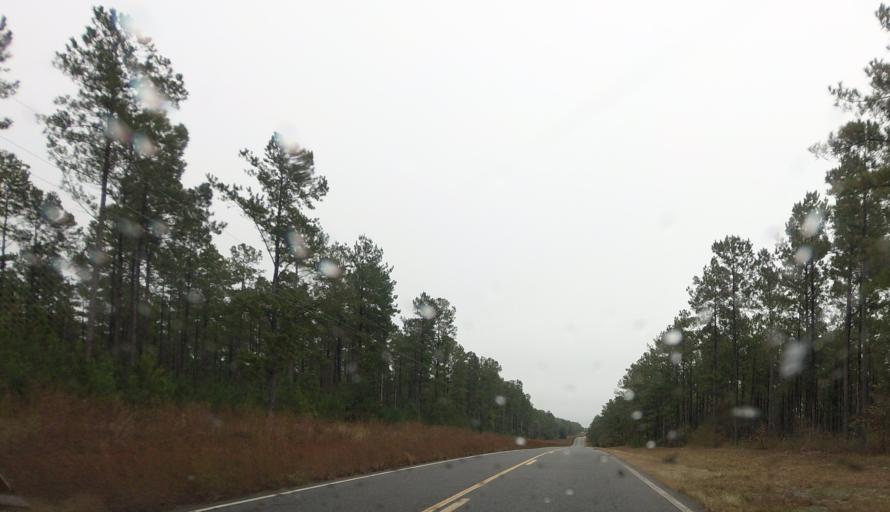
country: US
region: Georgia
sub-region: Taylor County
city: Butler
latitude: 32.4351
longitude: -84.3394
